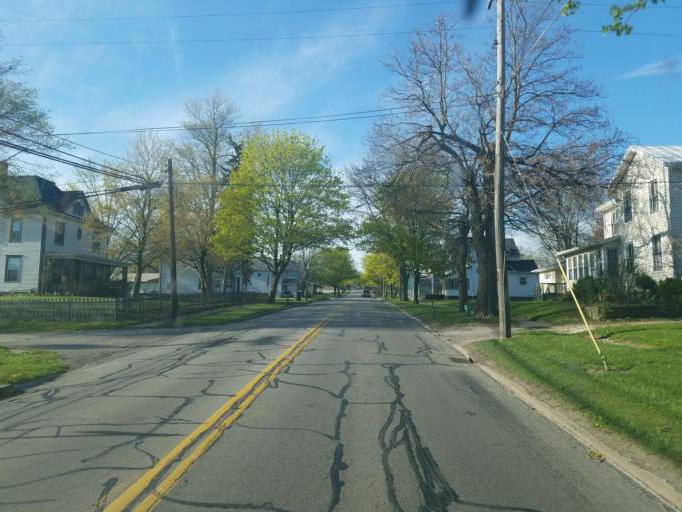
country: US
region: Ohio
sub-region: Ashland County
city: Ashland
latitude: 40.9623
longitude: -82.3647
